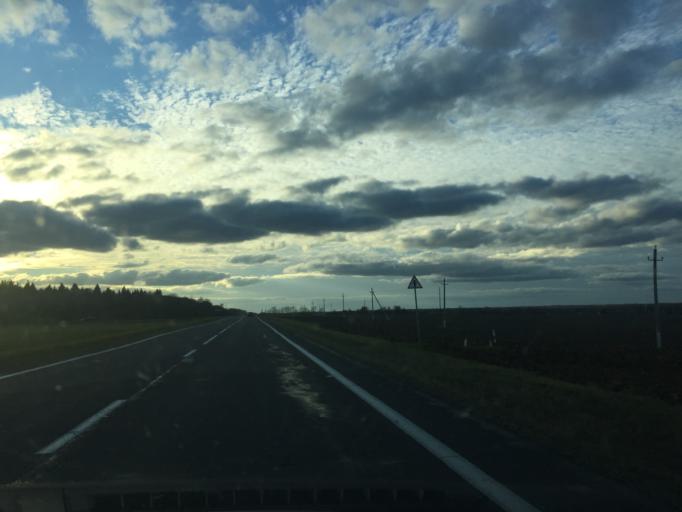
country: BY
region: Vitebsk
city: Vyerkhnyadzvinsk
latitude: 55.8234
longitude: 27.7567
